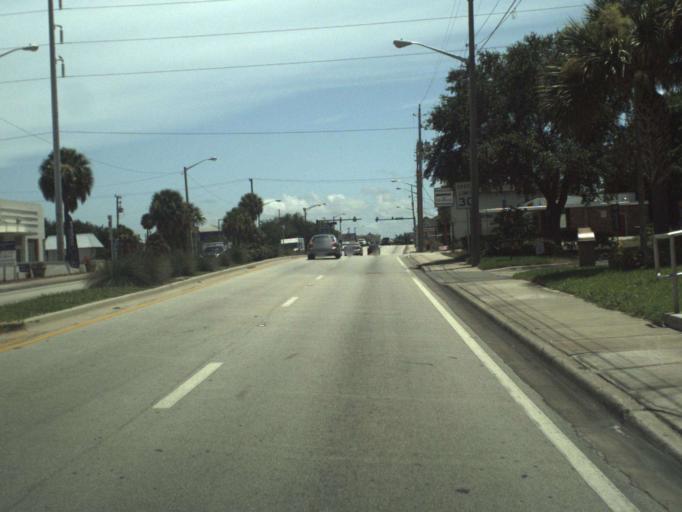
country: US
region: Florida
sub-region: Saint Lucie County
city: Fort Pierce
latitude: 27.4544
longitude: -80.3273
